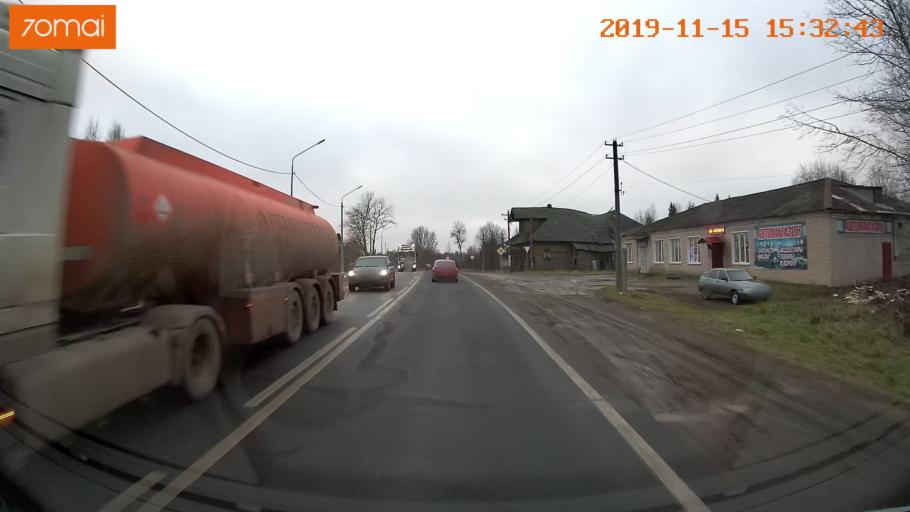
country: RU
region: Jaroslavl
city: Danilov
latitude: 58.0875
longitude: 40.0969
